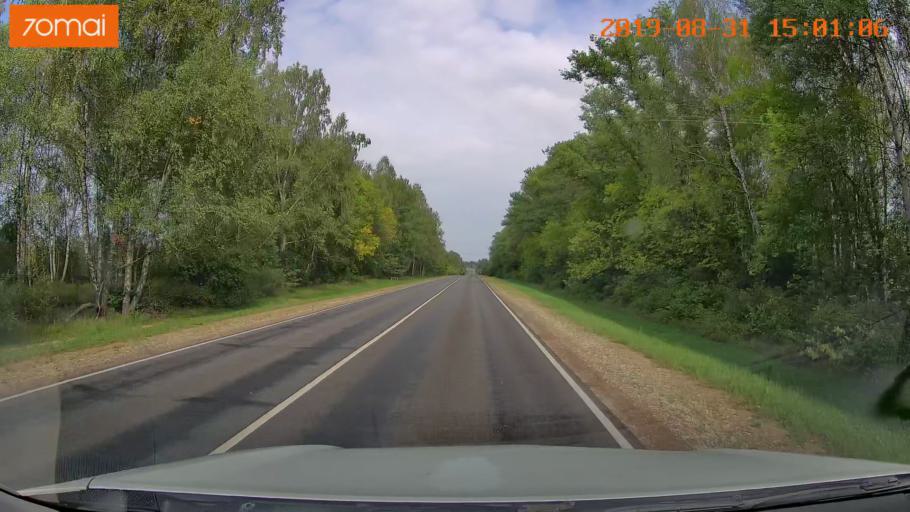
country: RU
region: Kaluga
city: Spas-Demensk
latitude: 54.3368
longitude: 34.0480
